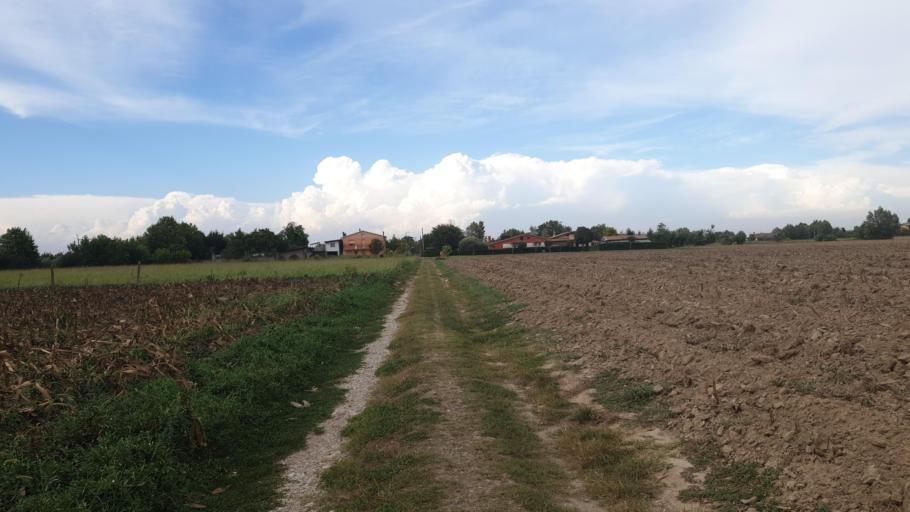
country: IT
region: Veneto
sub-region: Provincia di Padova
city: Bertipaglia
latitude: 45.3290
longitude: 11.8790
